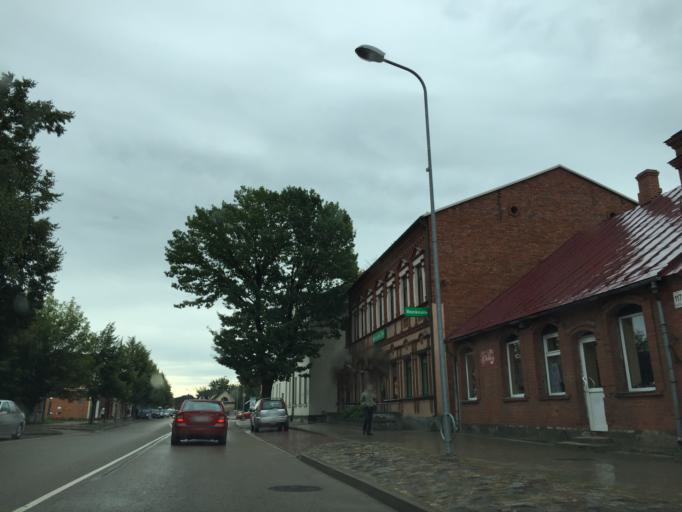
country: LV
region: Jekabpils Rajons
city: Jekabpils
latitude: 56.5020
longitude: 25.8713
